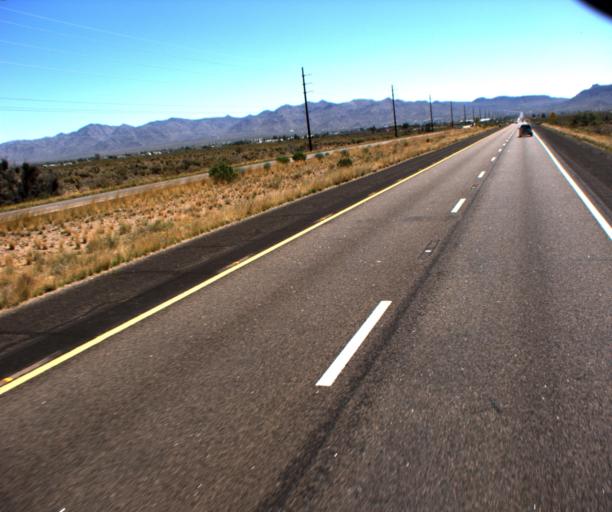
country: US
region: Arizona
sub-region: Mohave County
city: Golden Valley
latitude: 35.2227
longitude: -114.2325
